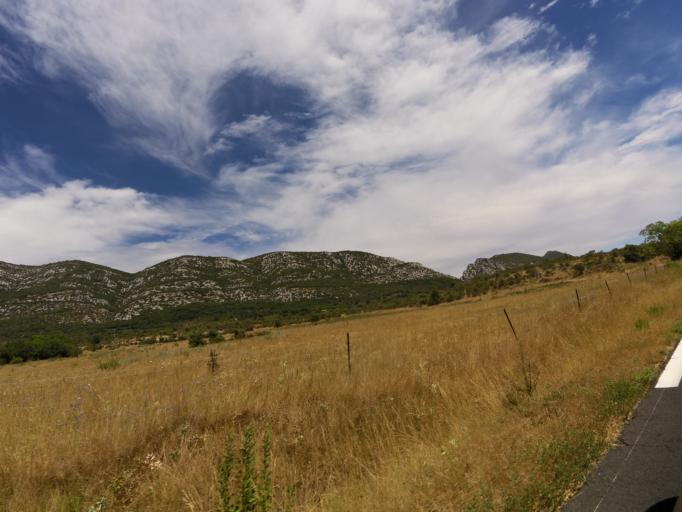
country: FR
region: Languedoc-Roussillon
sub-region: Departement du Gard
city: Saint-Hippolyte-du-Fort
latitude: 43.9500
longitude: 3.7883
